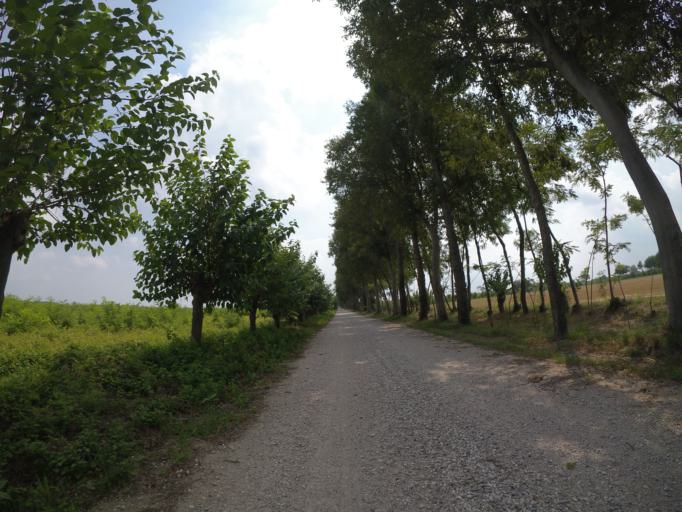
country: IT
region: Friuli Venezia Giulia
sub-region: Provincia di Udine
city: Sedegliano
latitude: 46.0123
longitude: 13.0106
